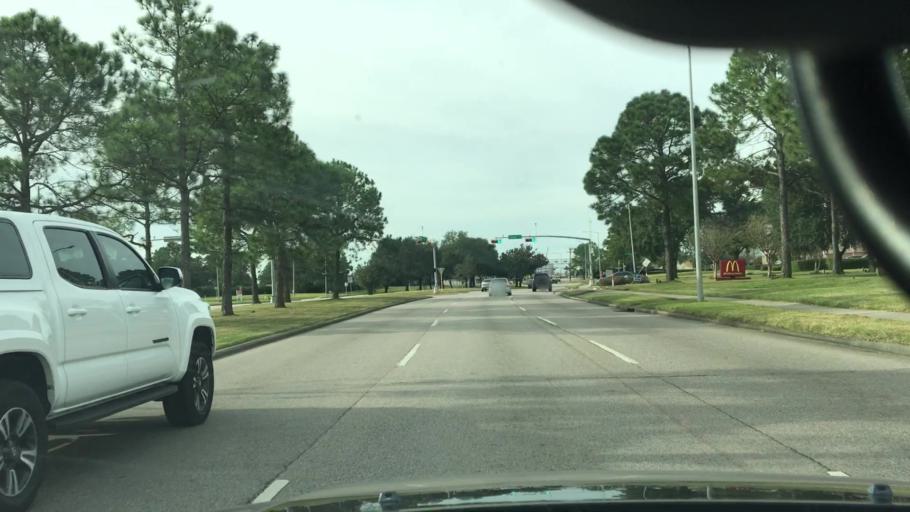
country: US
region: Texas
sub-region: Harris County
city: Webster
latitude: 29.5514
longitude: -95.1257
